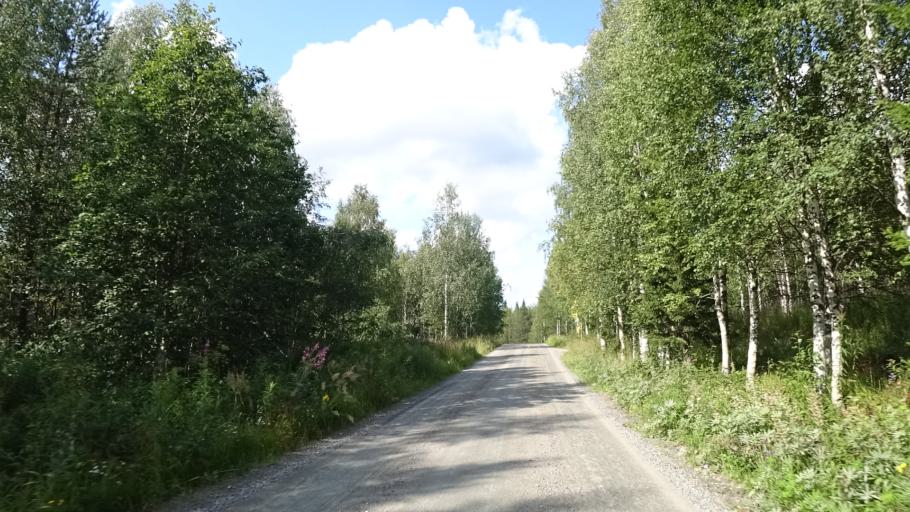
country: FI
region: North Karelia
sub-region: Joensuu
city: Ilomantsi
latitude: 62.9322
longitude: 31.3078
